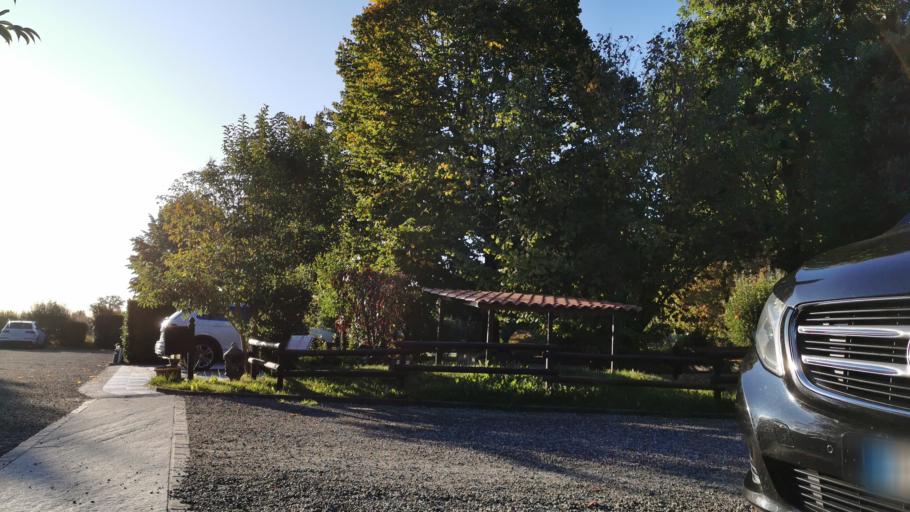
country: IT
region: Piedmont
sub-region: Provincia di Torino
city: San Francesco al Campo
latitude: 45.2232
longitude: 7.6631
